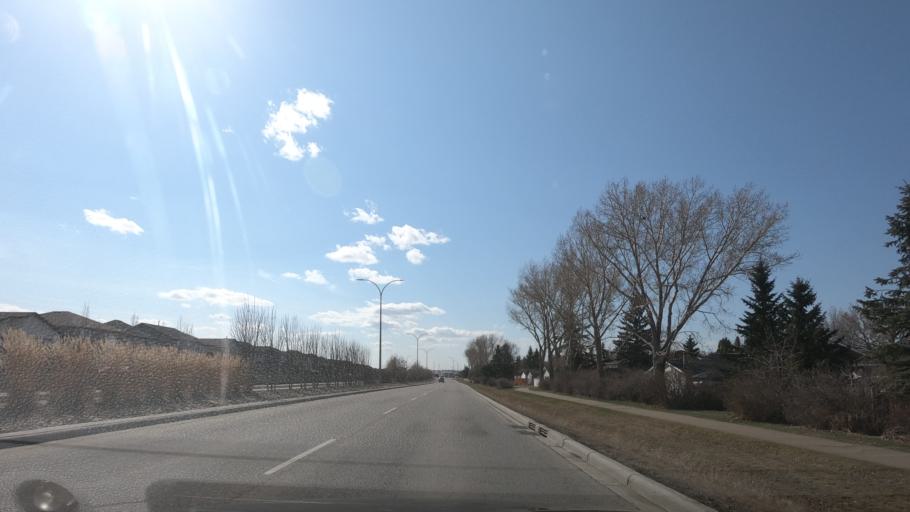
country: CA
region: Alberta
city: Airdrie
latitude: 51.2708
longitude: -113.9844
